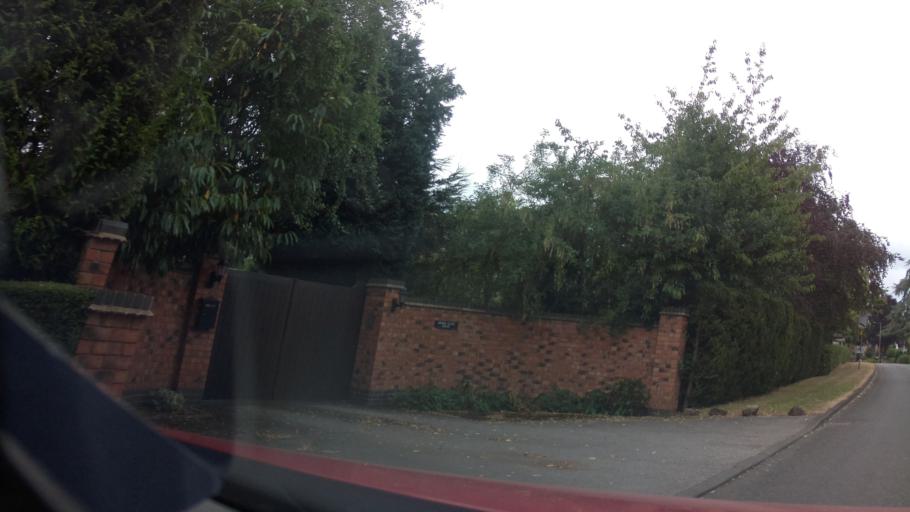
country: GB
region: England
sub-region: Derbyshire
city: Borrowash
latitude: 52.9066
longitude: -1.3639
